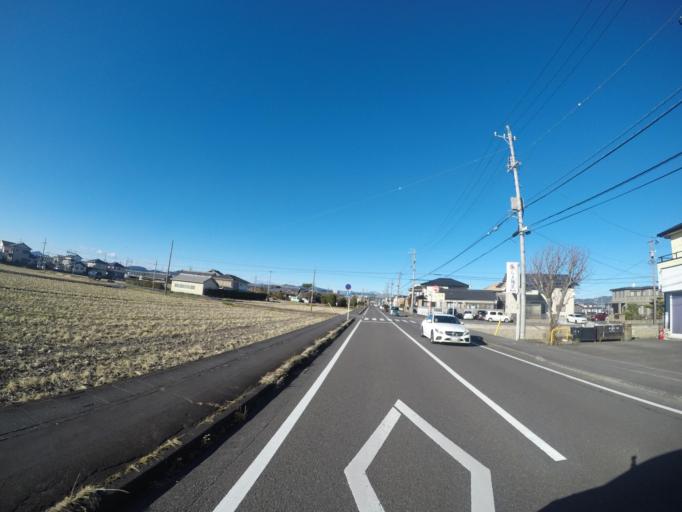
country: JP
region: Shizuoka
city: Fujieda
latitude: 34.8357
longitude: 138.2572
